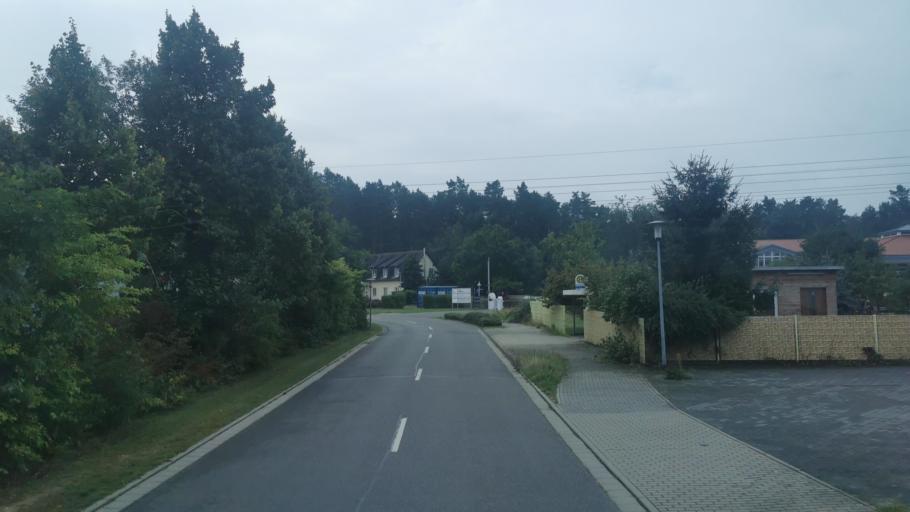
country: DE
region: Brandenburg
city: Kolkwitz
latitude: 51.7381
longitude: 14.2527
